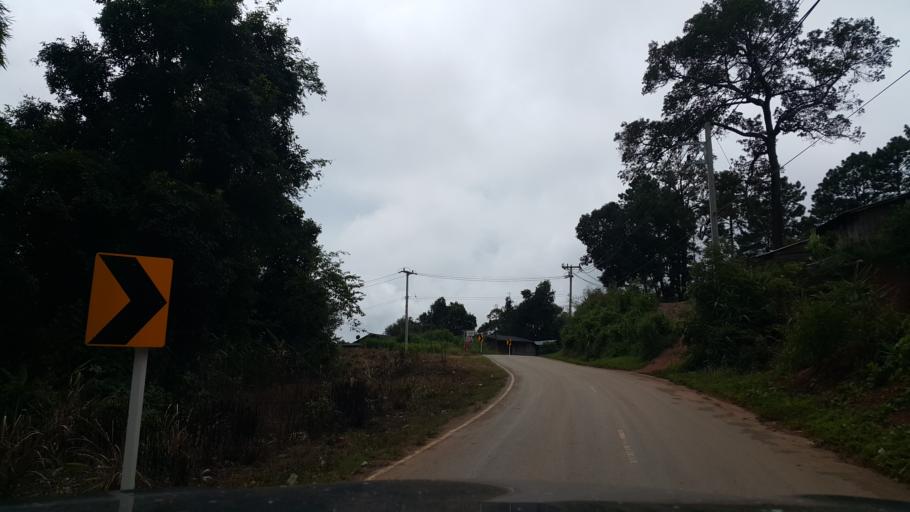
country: TH
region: Chiang Mai
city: Samoeng
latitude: 18.8806
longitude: 98.5094
